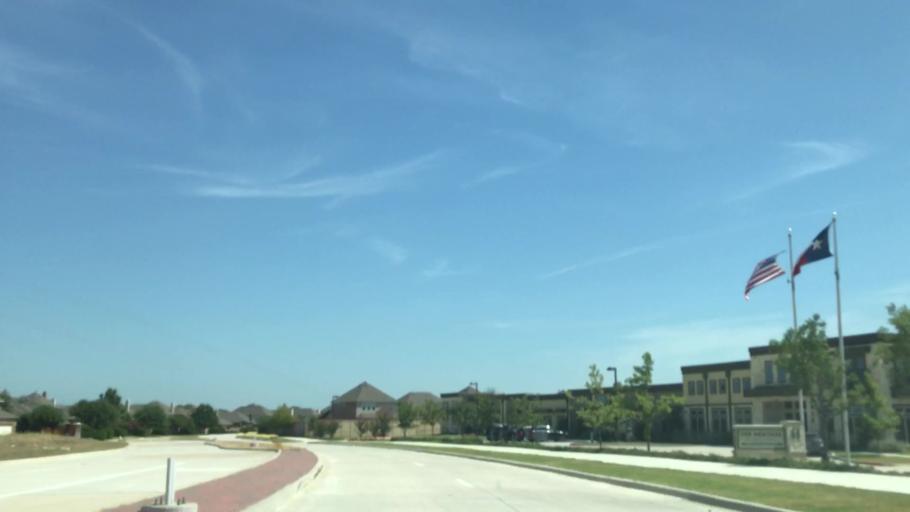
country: US
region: Texas
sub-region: Collin County
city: Allen
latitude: 33.1193
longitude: -96.6757
